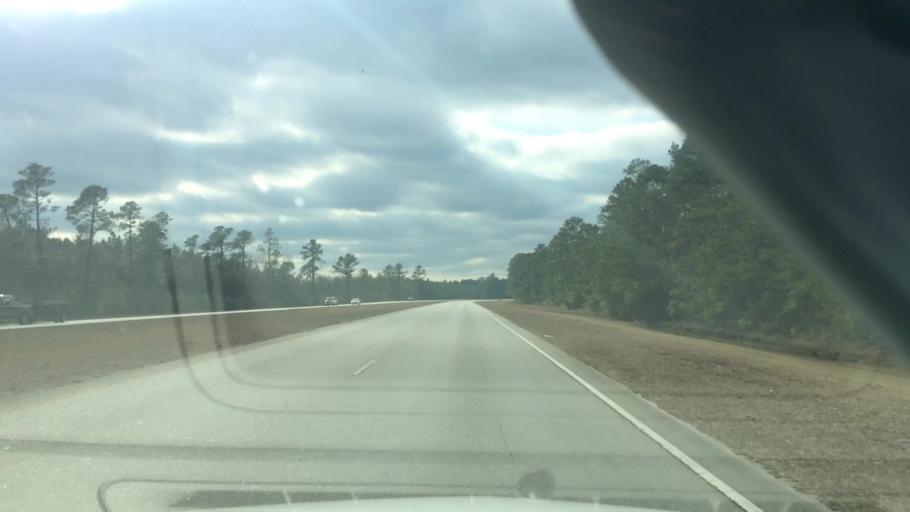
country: US
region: North Carolina
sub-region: Brunswick County
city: Bolivia
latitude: 34.0528
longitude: -78.2160
